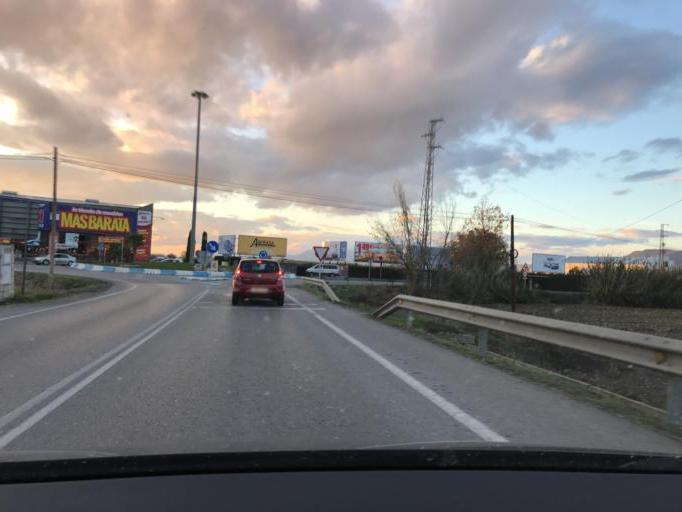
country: ES
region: Andalusia
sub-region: Provincia de Granada
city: Cullar-Vega
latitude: 37.1797
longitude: -3.6709
